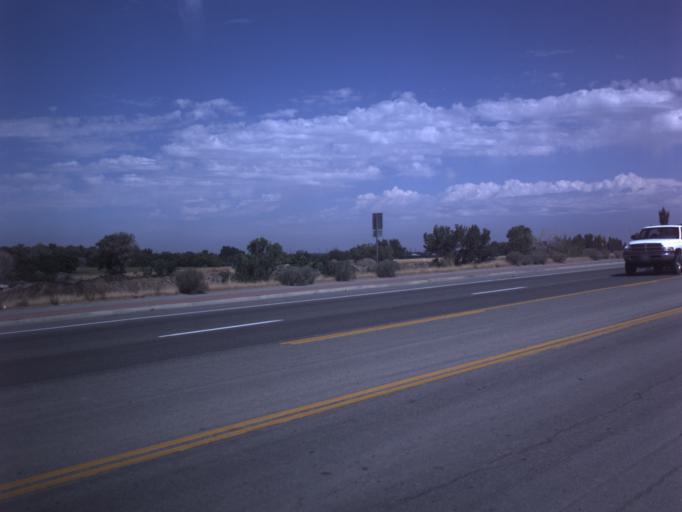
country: US
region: Utah
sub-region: Weber County
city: Marriott-Slaterville
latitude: 41.2428
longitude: -112.0253
